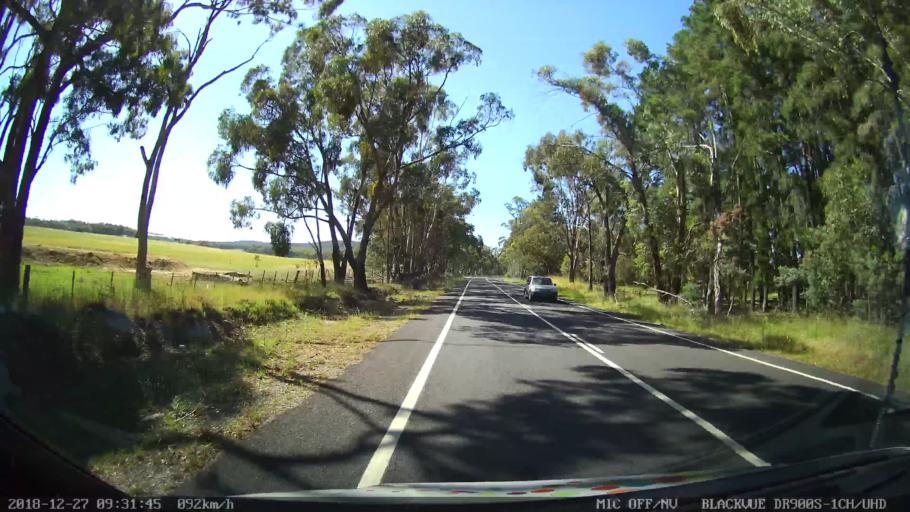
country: AU
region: New South Wales
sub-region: Lithgow
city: Portland
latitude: -33.1978
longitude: 150.0121
